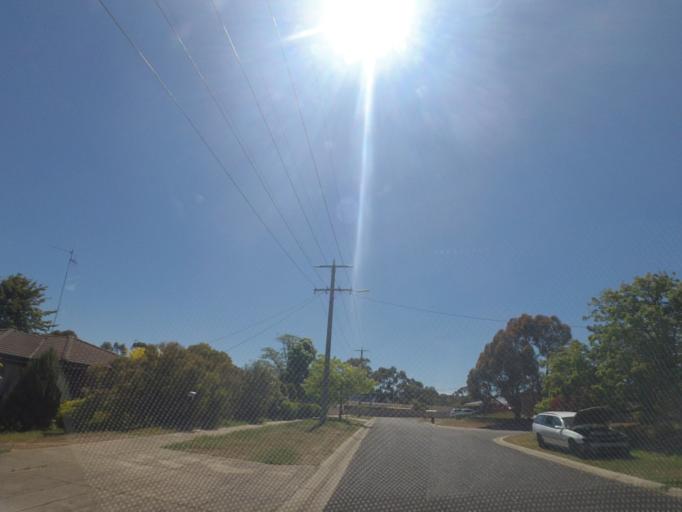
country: AU
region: Victoria
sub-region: Whittlesea
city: Whittlesea
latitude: -37.2078
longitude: 145.0617
